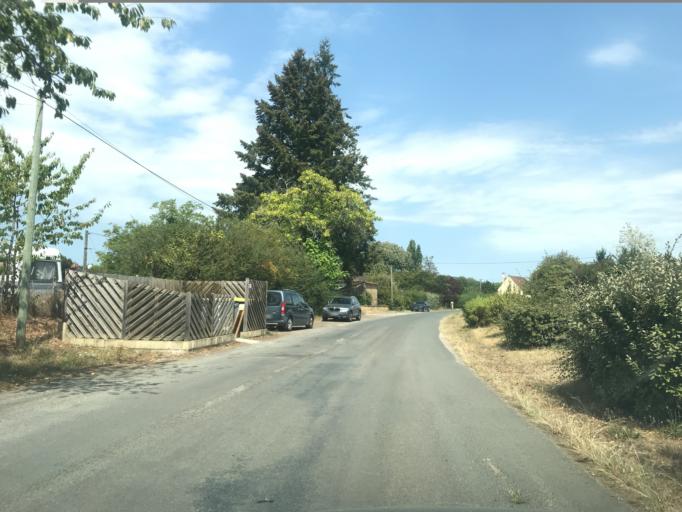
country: FR
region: Aquitaine
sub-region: Departement de la Dordogne
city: Carsac-Aillac
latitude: 44.8315
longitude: 1.2734
